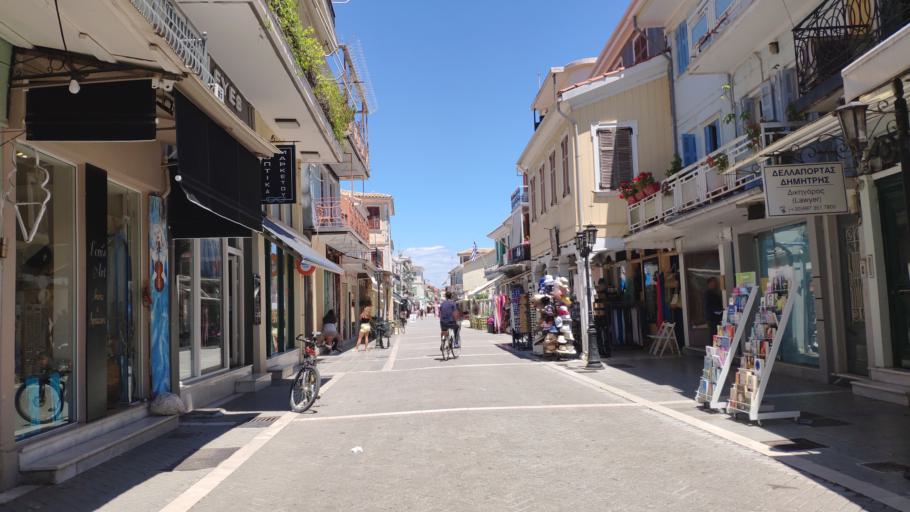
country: GR
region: Ionian Islands
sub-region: Lefkada
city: Lefkada
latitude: 38.8313
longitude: 20.7051
